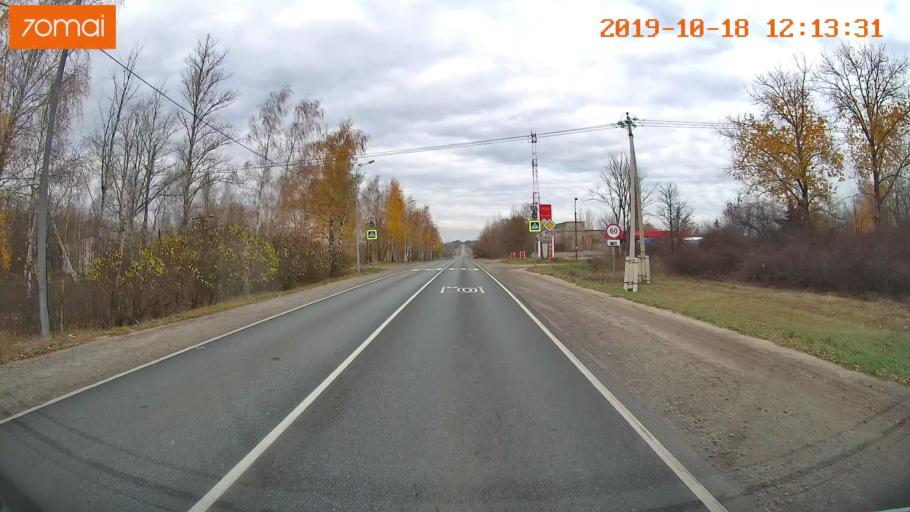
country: RU
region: Rjazan
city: Zakharovo
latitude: 54.4216
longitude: 39.3709
